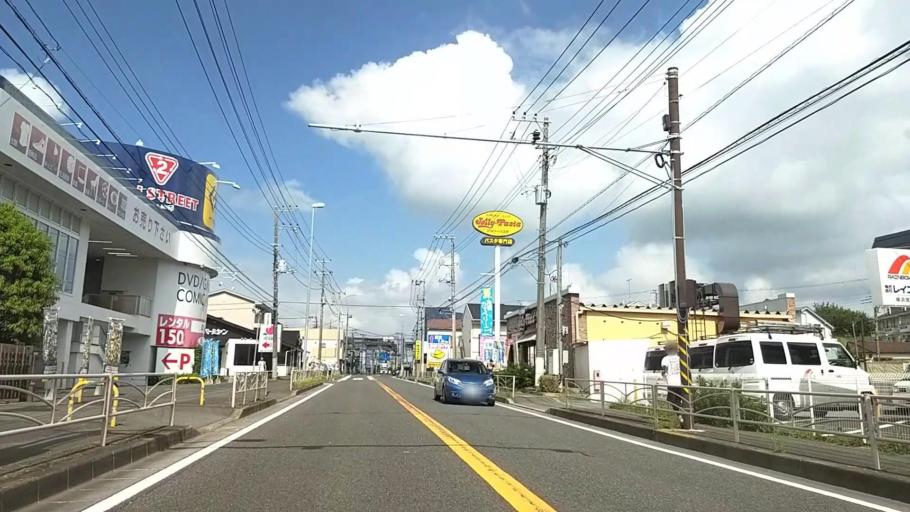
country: JP
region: Kanagawa
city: Minami-rinkan
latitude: 35.4835
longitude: 139.5271
